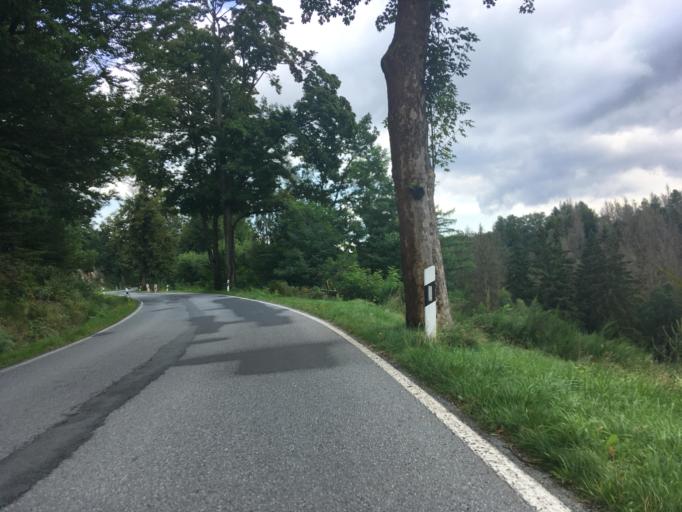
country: CZ
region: Ustecky
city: Mikulasovice
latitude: 50.9248
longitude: 14.3446
